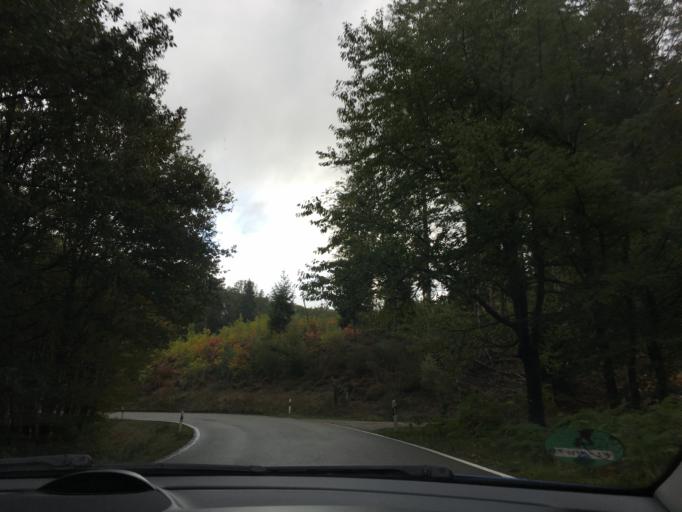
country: DE
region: Rheinland-Pfalz
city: Geiselberg
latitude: 49.3467
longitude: 7.7084
